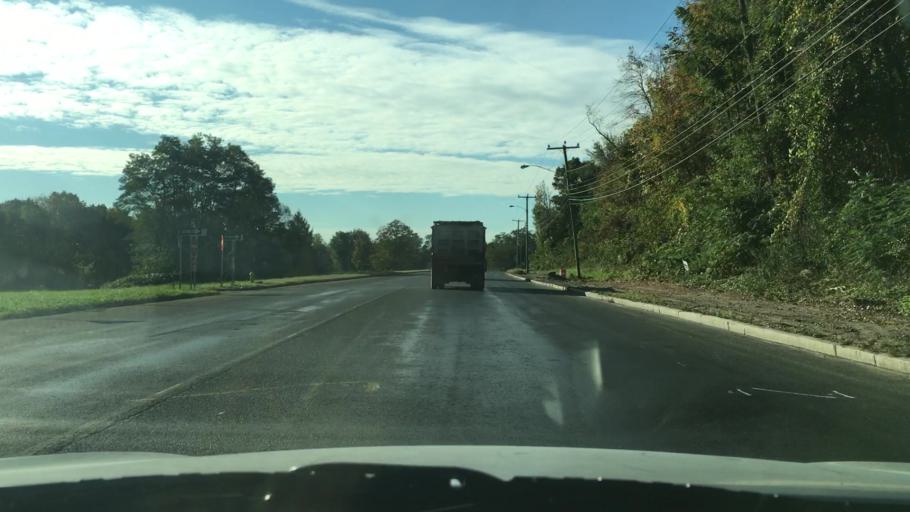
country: US
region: Massachusetts
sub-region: Hampden County
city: Agawam
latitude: 42.0575
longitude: -72.6758
